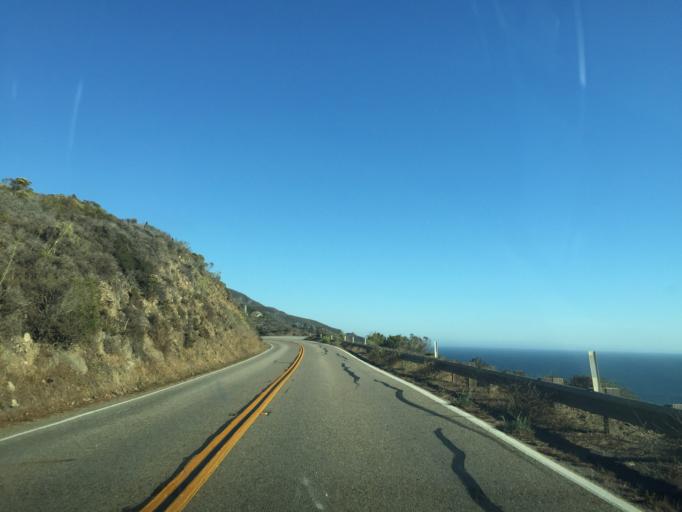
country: US
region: California
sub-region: Monterey County
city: King City
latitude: 35.8835
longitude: -121.4563
